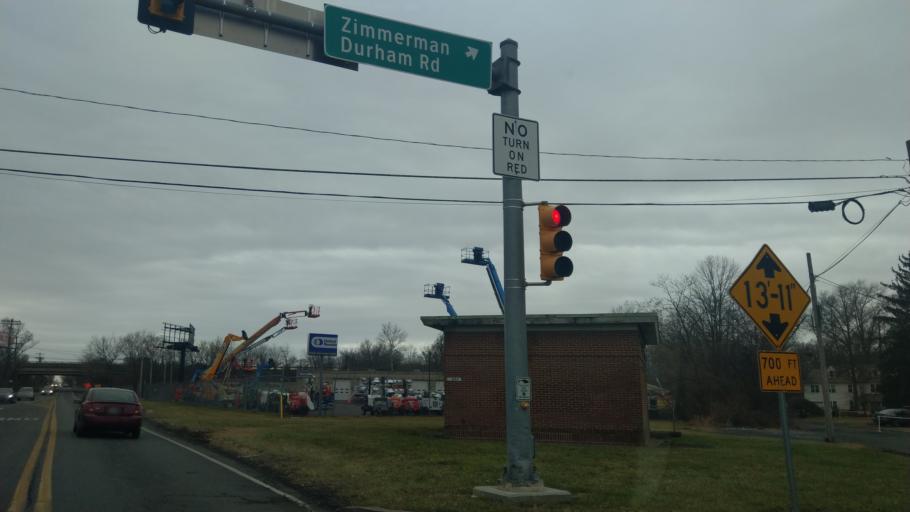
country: US
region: Pennsylvania
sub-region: Bucks County
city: Hulmeville
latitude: 40.1319
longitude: -74.8882
